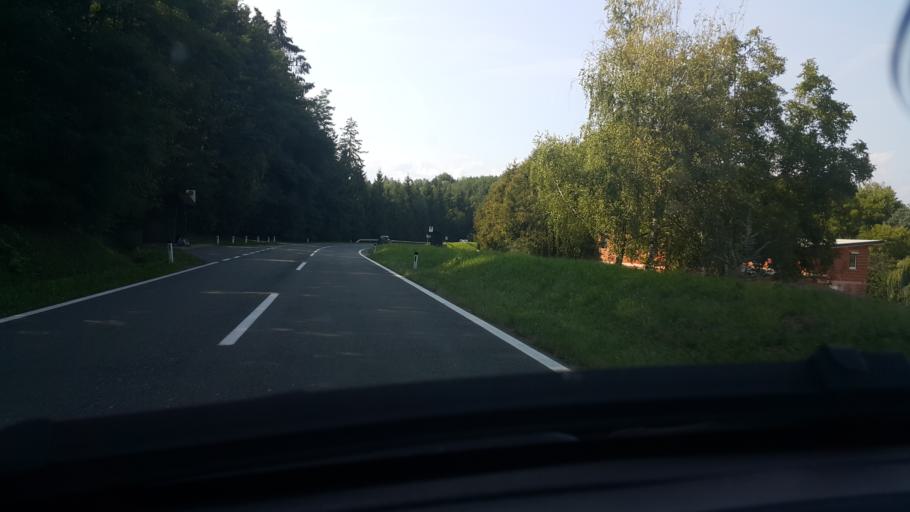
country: AT
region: Styria
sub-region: Politischer Bezirk Graz-Umgebung
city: Thal
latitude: 47.0628
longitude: 15.3338
